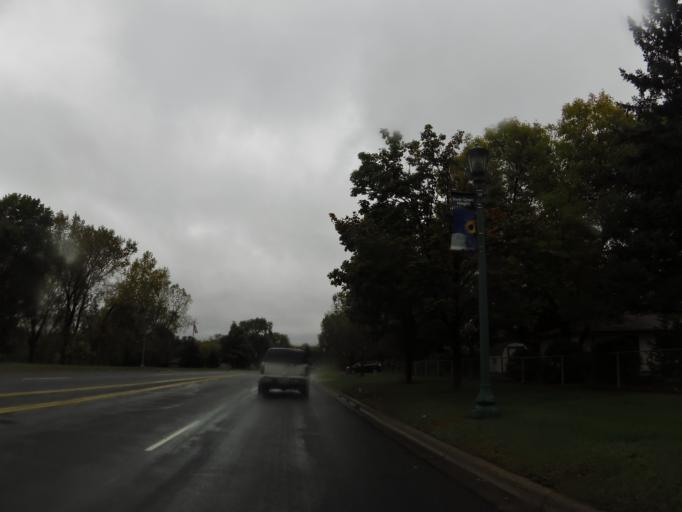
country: US
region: Minnesota
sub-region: Dakota County
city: Inver Grove Heights
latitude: 44.8488
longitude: -93.0431
